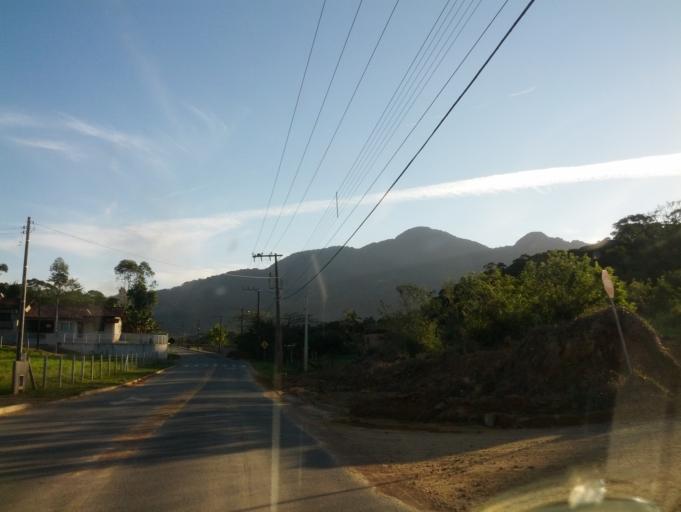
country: BR
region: Santa Catarina
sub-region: Indaial
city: Indaial
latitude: -26.9075
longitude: -49.2629
